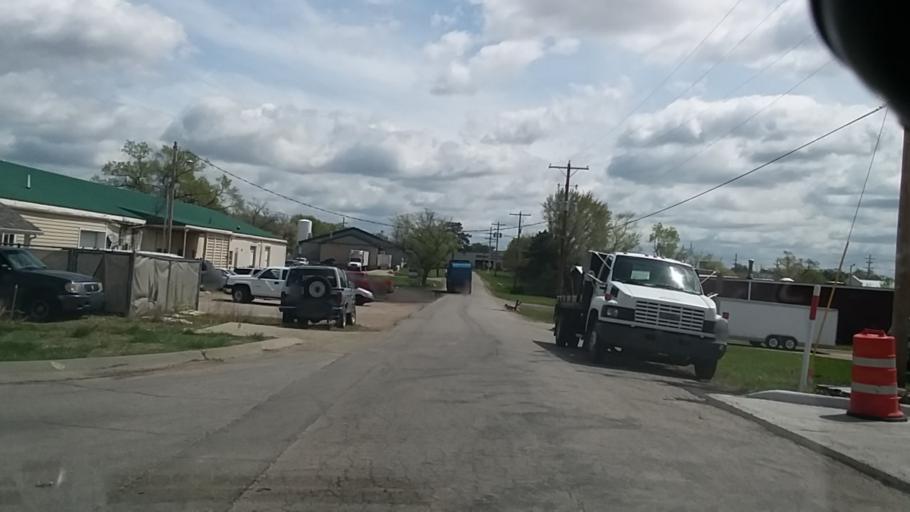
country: US
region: Kansas
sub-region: Douglas County
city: Lawrence
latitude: 38.9439
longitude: -95.2259
